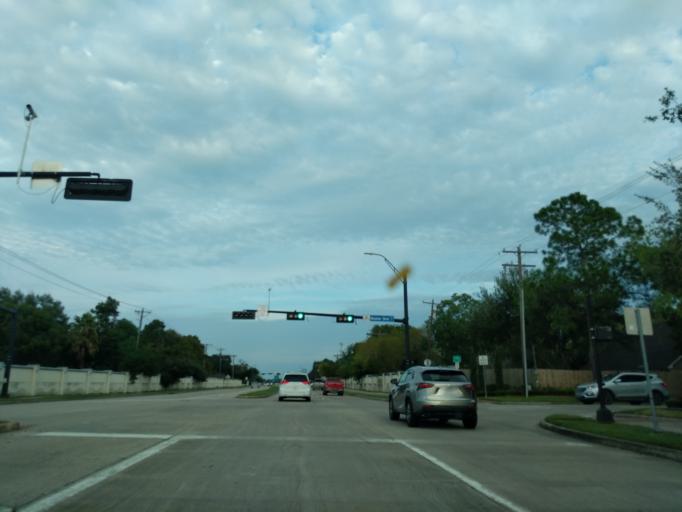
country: US
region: Texas
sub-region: Galveston County
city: Clear Lake Shores
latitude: 29.5249
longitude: -95.0579
